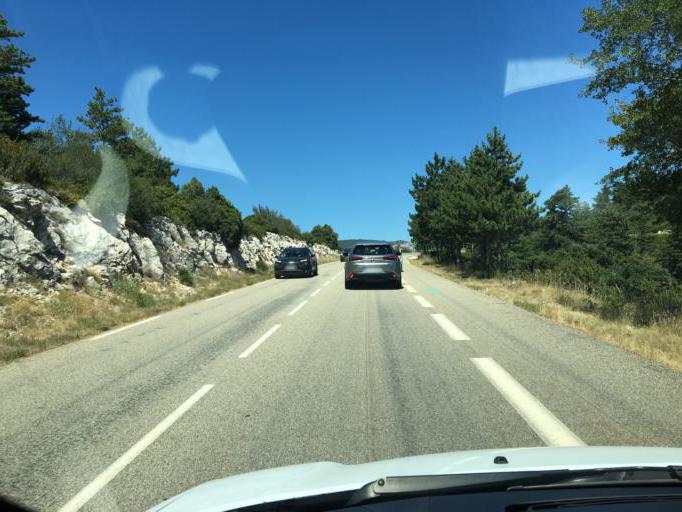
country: FR
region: Provence-Alpes-Cote d'Azur
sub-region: Departement du Vaucluse
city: Bedoin
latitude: 44.1686
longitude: 5.1899
